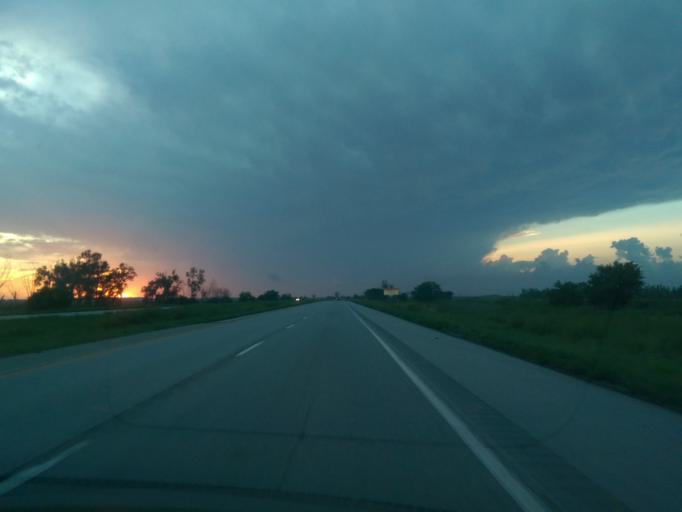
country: US
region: Iowa
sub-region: Fremont County
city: Hamburg
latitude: 40.6186
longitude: -95.6997
